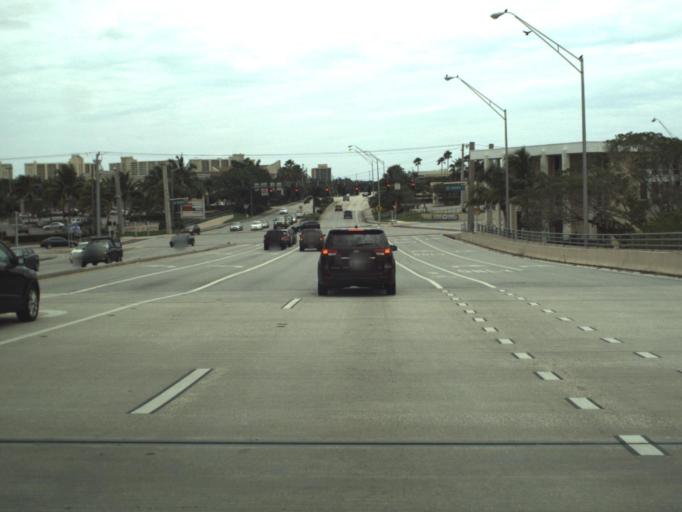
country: US
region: Florida
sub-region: Palm Beach County
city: Jupiter
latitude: 26.9338
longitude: -80.0823
